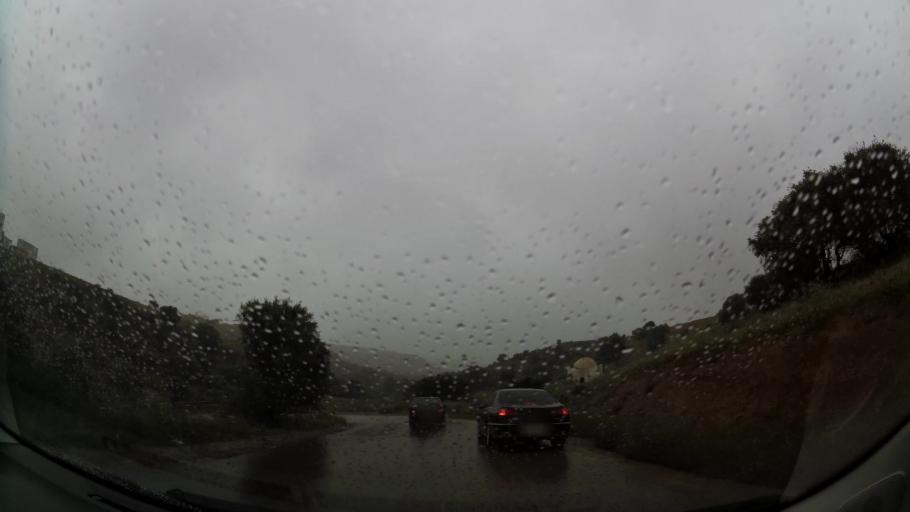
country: MA
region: Oriental
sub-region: Nador
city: Boudinar
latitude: 35.1235
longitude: -3.6351
